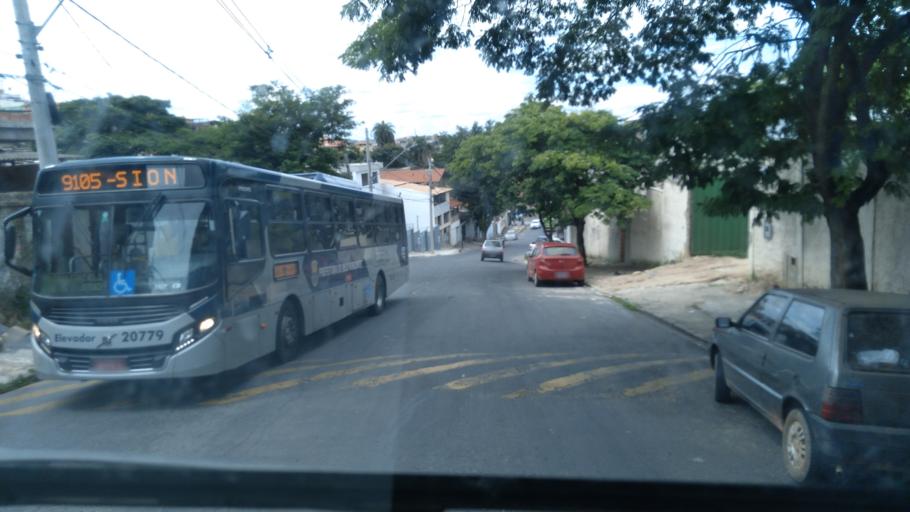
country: BR
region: Minas Gerais
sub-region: Belo Horizonte
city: Belo Horizonte
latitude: -19.8850
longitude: -43.8943
